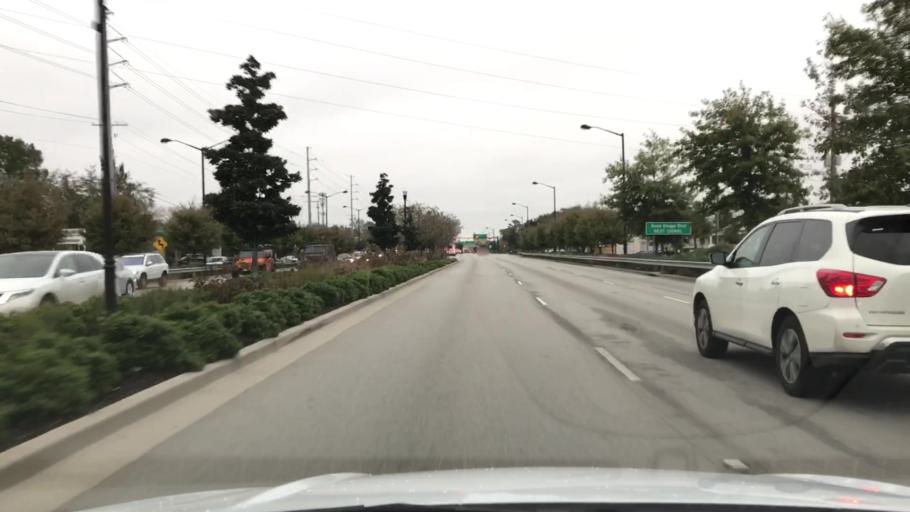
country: US
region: South Carolina
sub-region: Charleston County
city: Mount Pleasant
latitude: 32.8112
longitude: -79.8672
